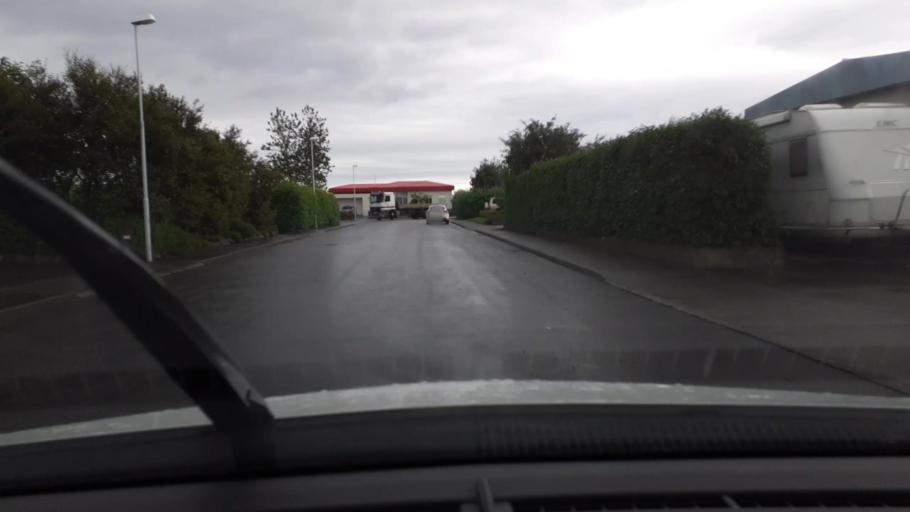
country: IS
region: West
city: Akranes
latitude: 64.3157
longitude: -22.0450
